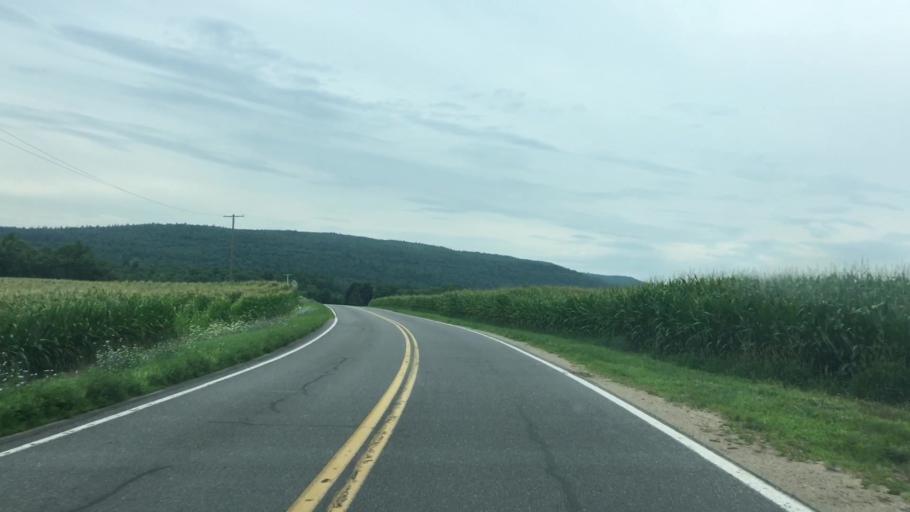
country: US
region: New York
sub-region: Clinton County
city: Peru
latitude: 44.5337
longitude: -73.5740
